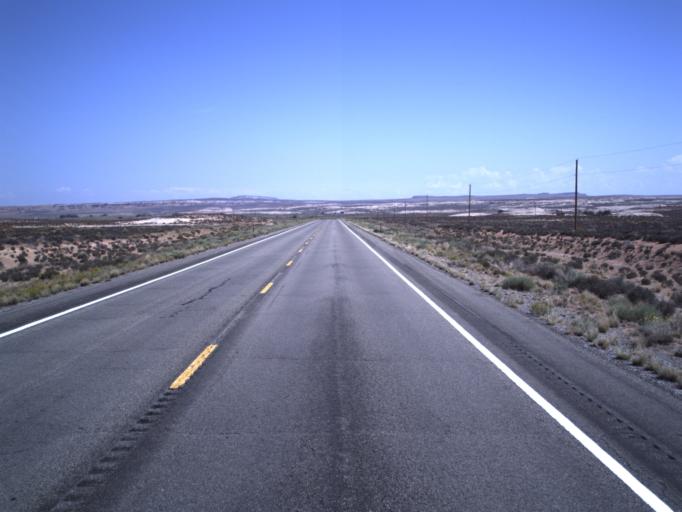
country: US
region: Utah
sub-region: San Juan County
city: Blanding
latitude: 37.0661
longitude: -109.5566
